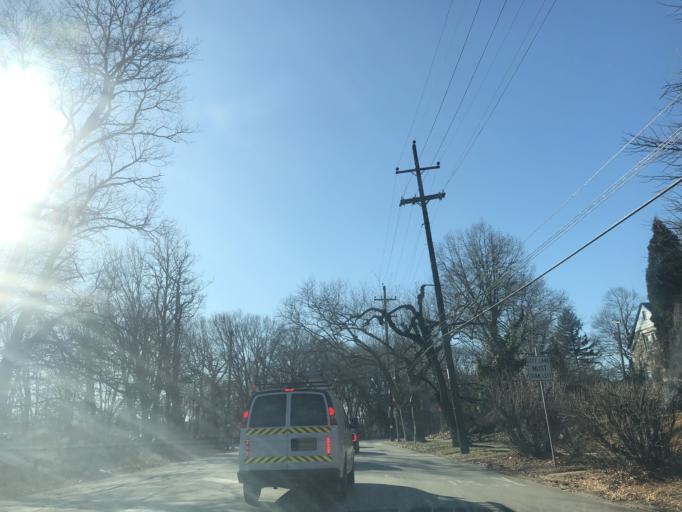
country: US
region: Pennsylvania
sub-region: Montgomery County
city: Bala-Cynwyd
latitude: 39.9910
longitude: -75.2199
